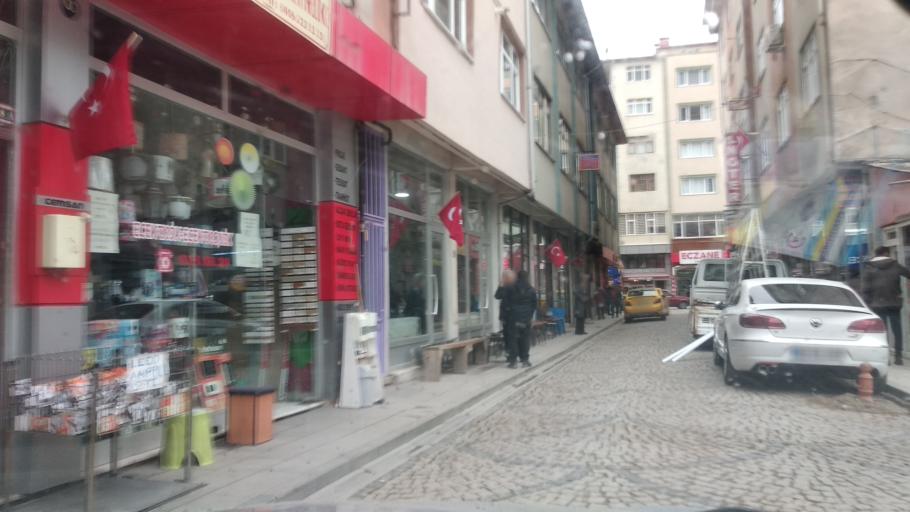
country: TR
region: Gumushane
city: Gumushkhane
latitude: 40.4584
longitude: 39.4791
